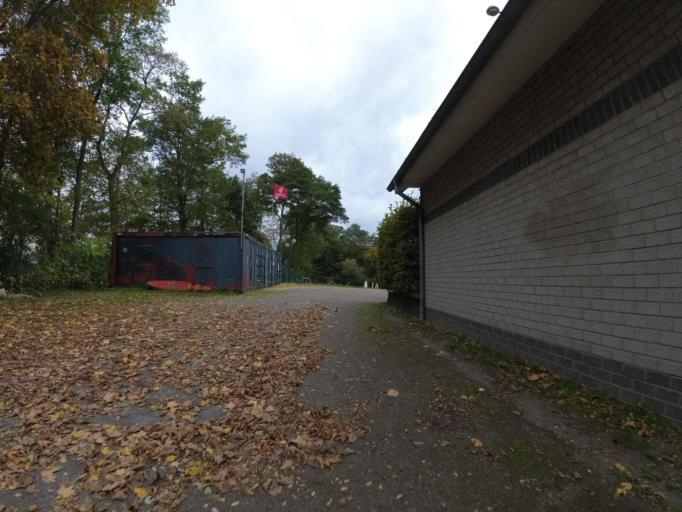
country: DE
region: North Rhine-Westphalia
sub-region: Regierungsbezirk Dusseldorf
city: Hochfeld
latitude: 51.3971
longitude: 6.6843
